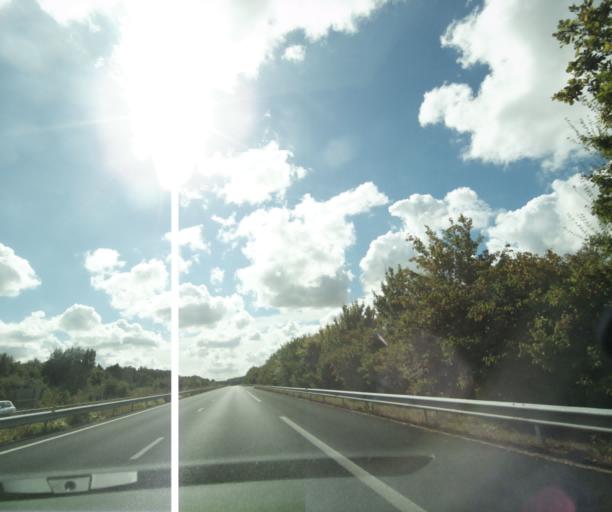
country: FR
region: Poitou-Charentes
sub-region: Departement de la Charente-Maritime
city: Cabariot
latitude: 45.9302
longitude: -0.8368
